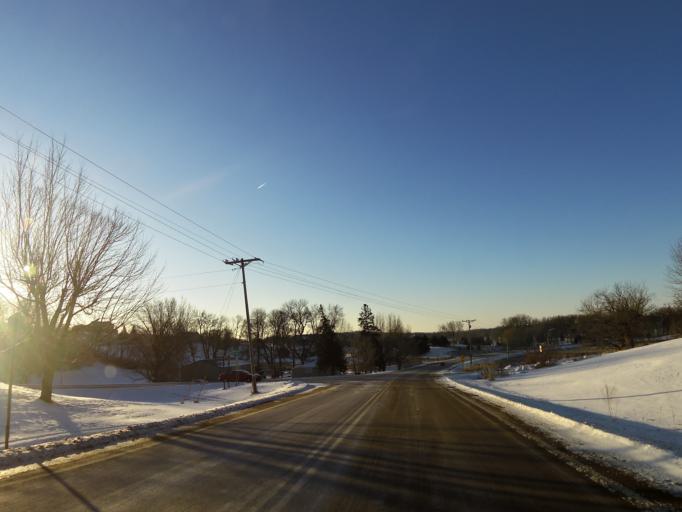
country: US
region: Minnesota
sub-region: Scott County
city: Prior Lake
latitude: 44.6600
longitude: -93.4602
